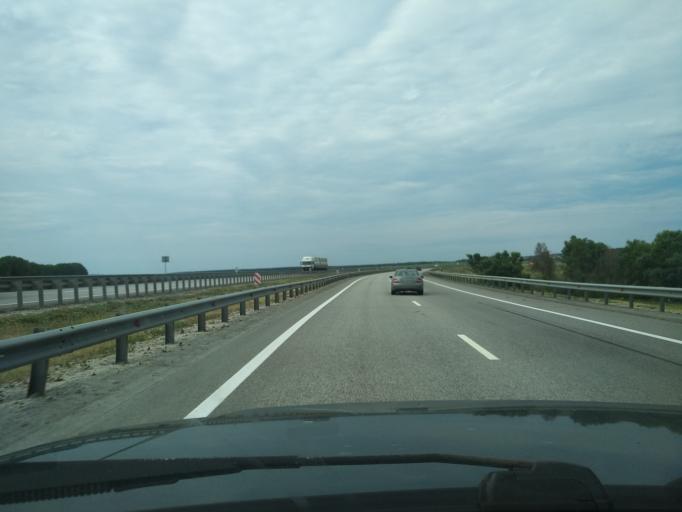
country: RU
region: Lipetsk
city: Khlevnoye
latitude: 52.0641
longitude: 39.1800
